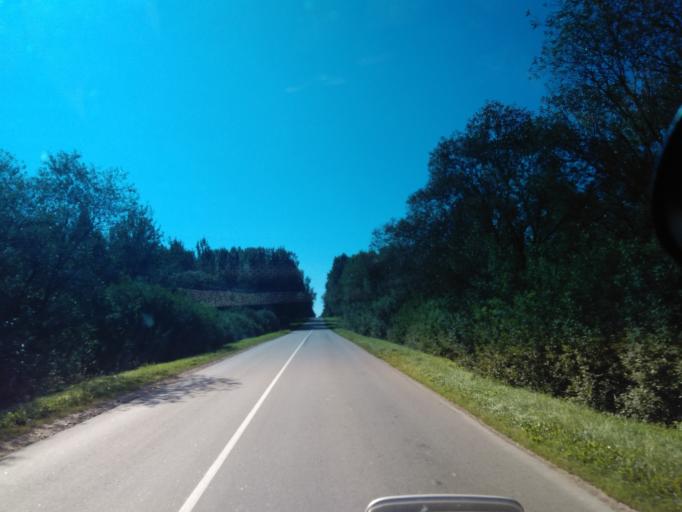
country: BY
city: Fanipol
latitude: 53.7071
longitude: 27.3490
